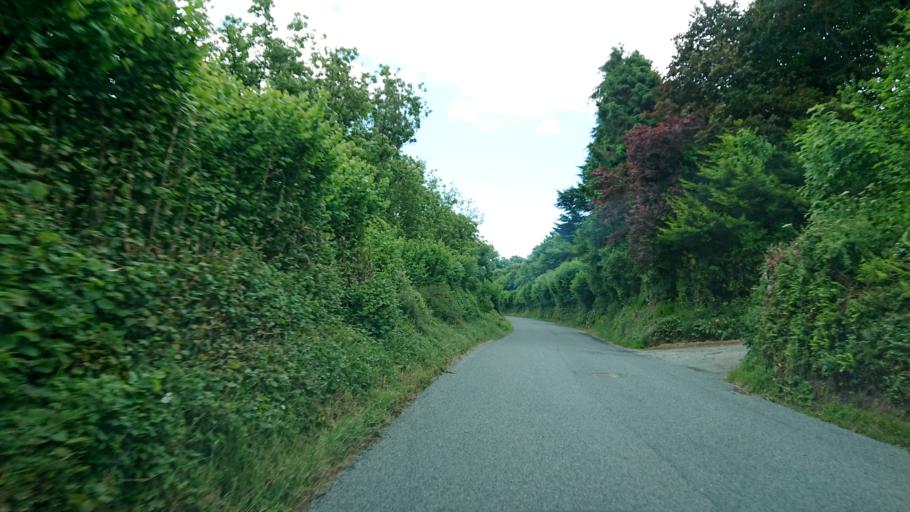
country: IE
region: Munster
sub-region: Waterford
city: Tra Mhor
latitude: 52.1780
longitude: -7.1504
